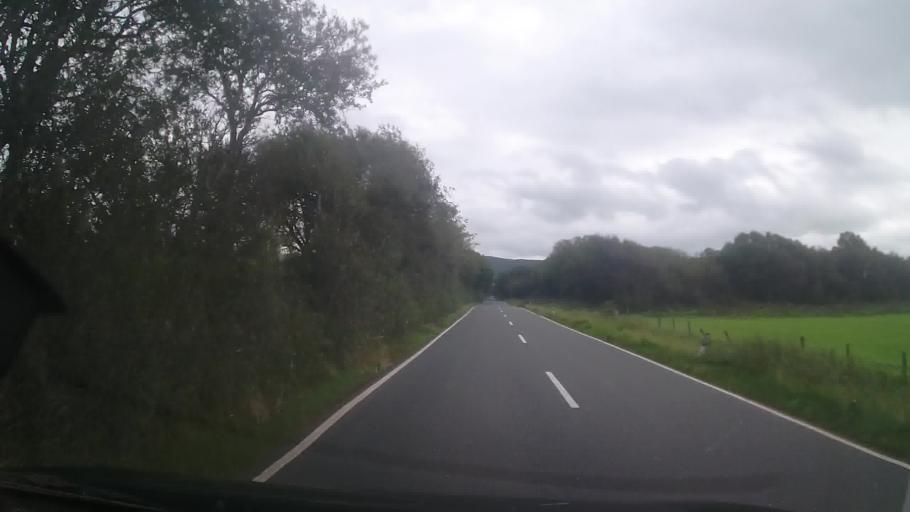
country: GB
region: Wales
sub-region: County of Ceredigion
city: Bow Street
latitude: 52.5151
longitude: -4.0121
